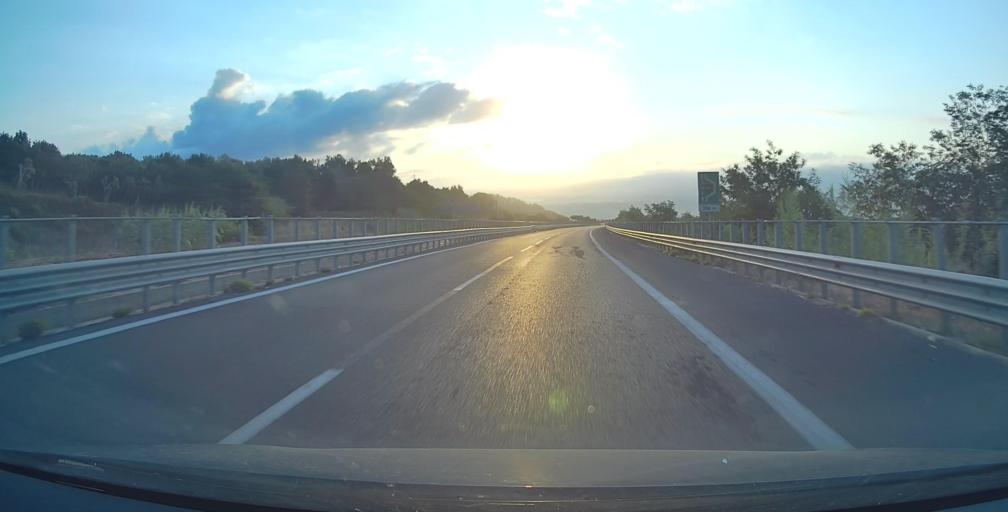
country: IT
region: Calabria
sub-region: Provincia di Reggio Calabria
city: Palmi
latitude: 38.3822
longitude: 15.8815
